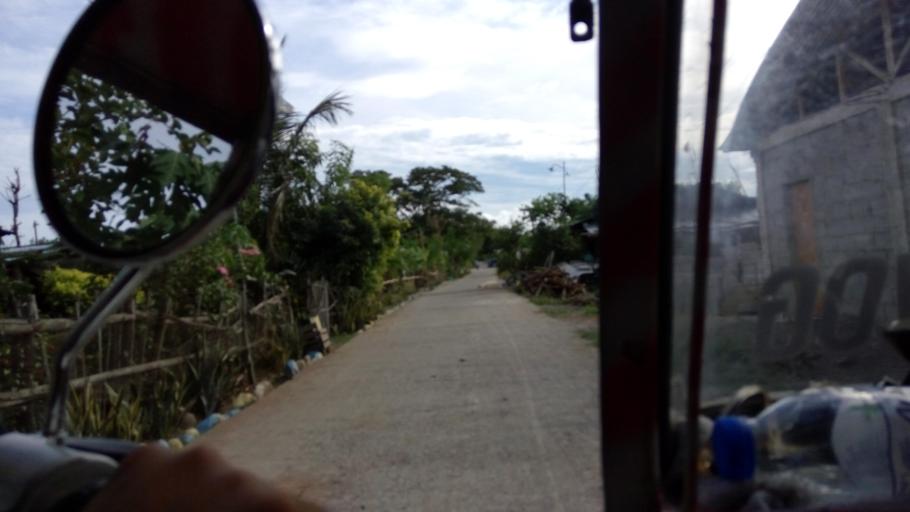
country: PH
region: Ilocos
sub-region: Province of La Union
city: San Eugenio
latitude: 16.3565
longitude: 120.3526
